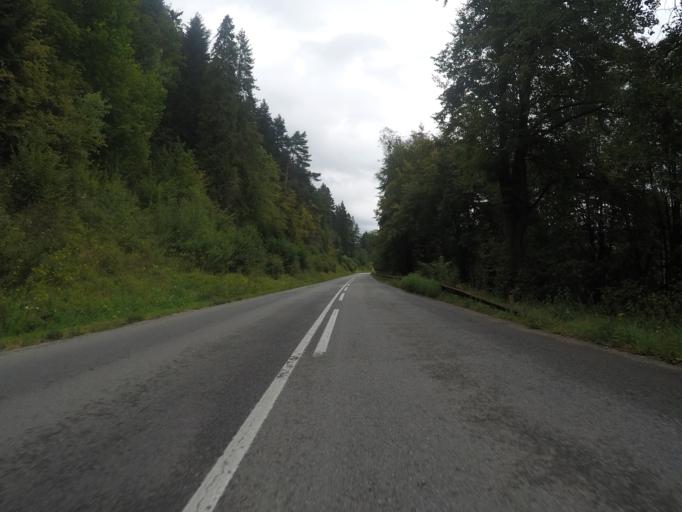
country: SK
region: Kosicky
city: Spisska Nova Ves
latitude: 48.9117
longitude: 20.5289
